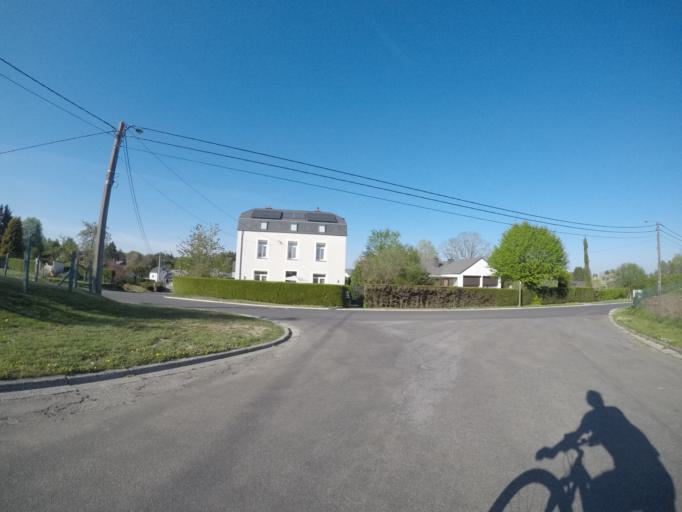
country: BE
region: Wallonia
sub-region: Province du Luxembourg
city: Tintigny
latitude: 49.7175
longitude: 5.5562
